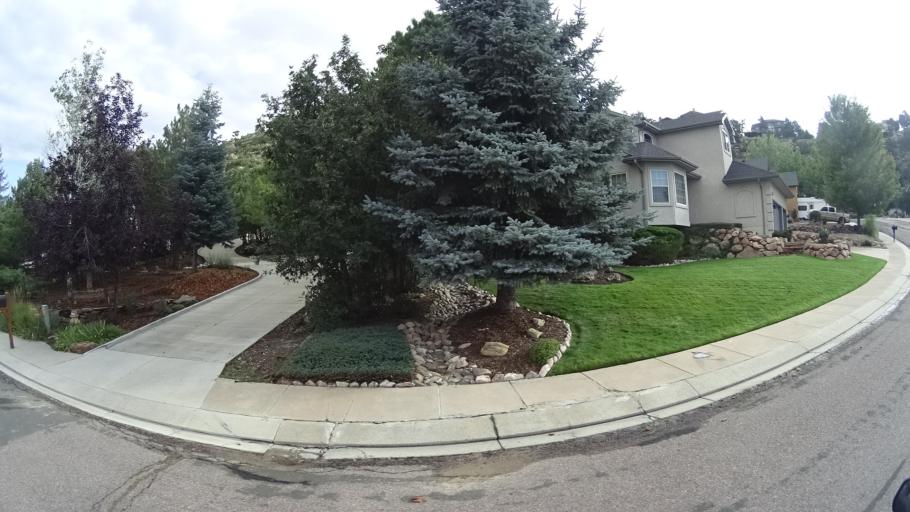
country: US
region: Colorado
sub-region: El Paso County
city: Manitou Springs
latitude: 38.9074
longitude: -104.8540
